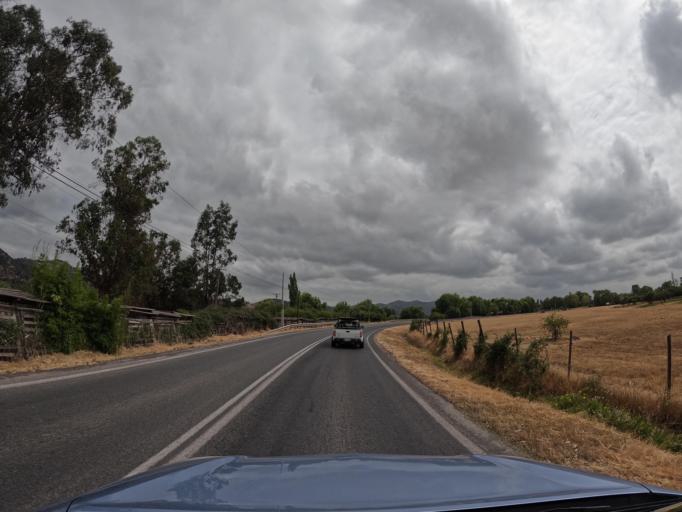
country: CL
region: Maule
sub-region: Provincia de Curico
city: Teno
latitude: -34.8507
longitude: -71.1928
